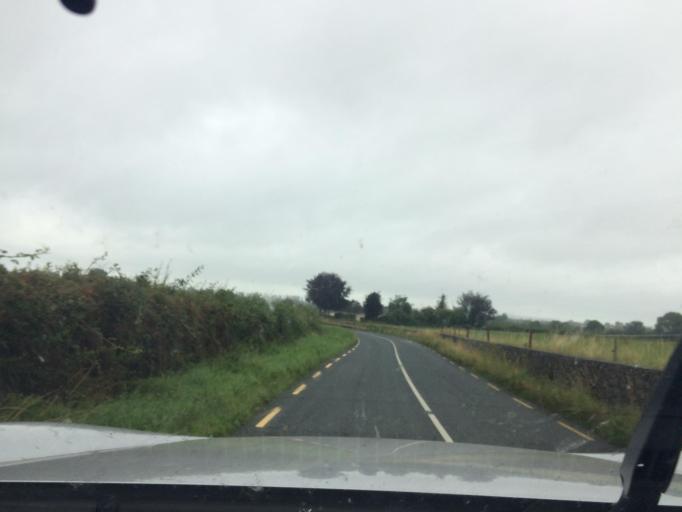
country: IE
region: Munster
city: Cashel
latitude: 52.5274
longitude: -7.8891
